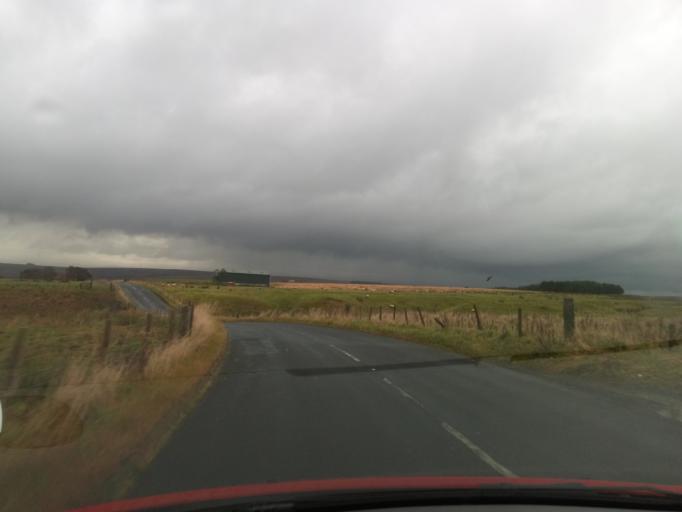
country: GB
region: England
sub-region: Northumberland
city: Corsenside
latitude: 55.1642
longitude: -2.2649
